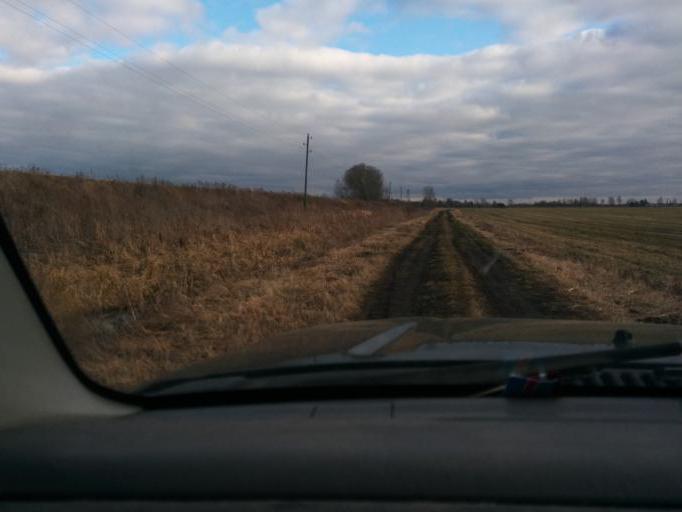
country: LV
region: Jelgava
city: Jelgava
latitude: 56.6903
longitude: 23.6873
